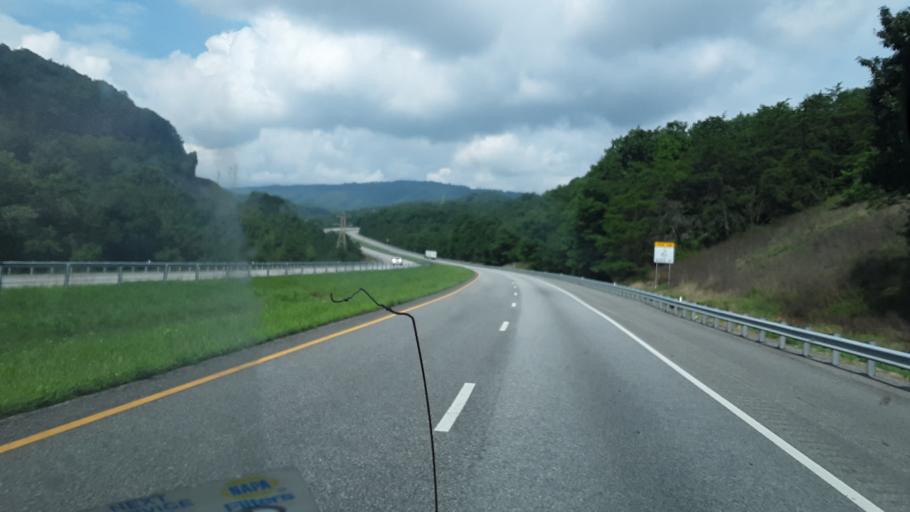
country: US
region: Virginia
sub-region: City of Covington
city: Covington
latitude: 37.7865
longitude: -80.0178
